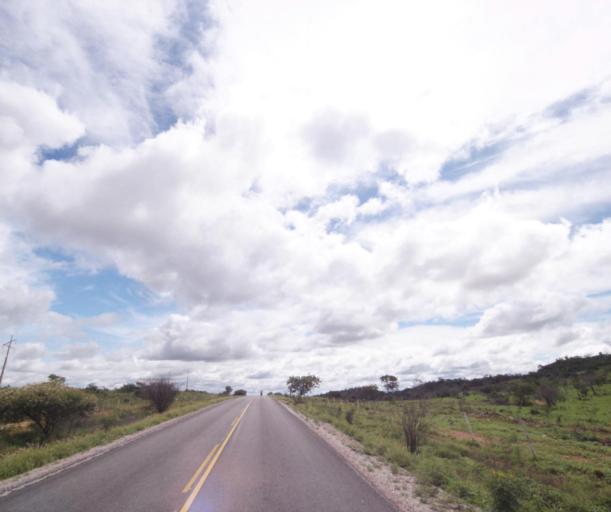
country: BR
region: Bahia
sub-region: Brumado
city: Brumado
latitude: -14.1554
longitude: -41.5171
